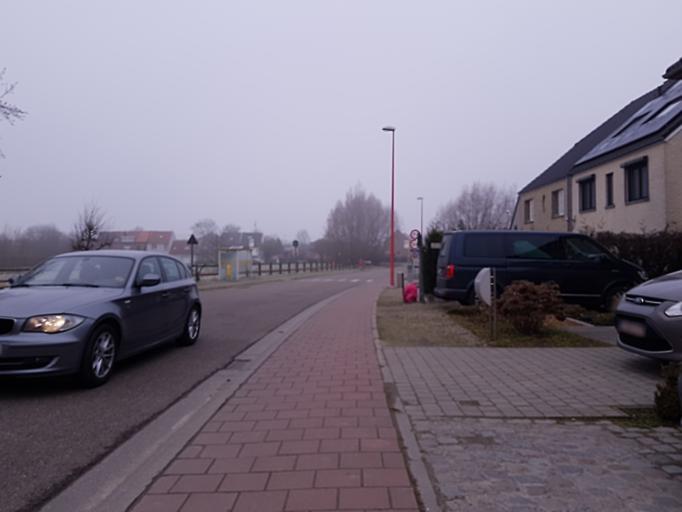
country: BE
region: Flanders
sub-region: Provincie Vlaams-Brabant
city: Grimbergen
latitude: 50.9437
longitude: 4.3984
